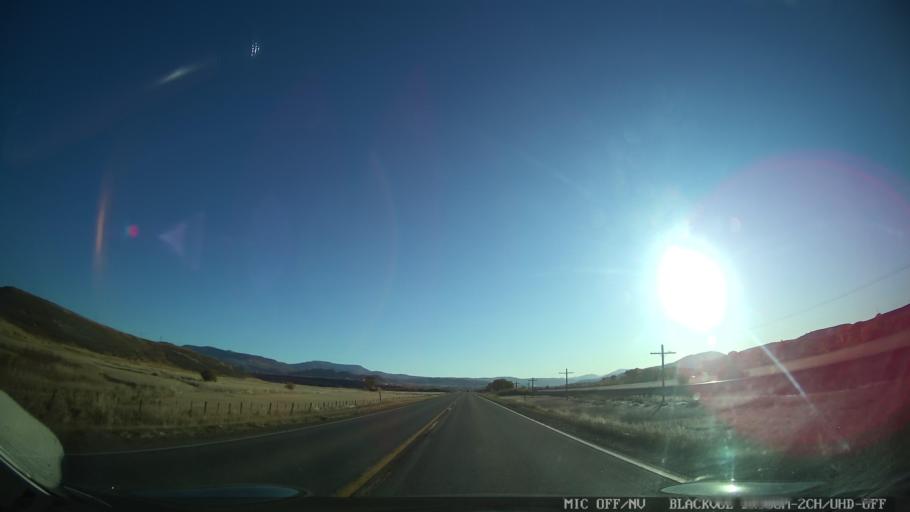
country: US
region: Colorado
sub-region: Grand County
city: Kremmling
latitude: 40.0570
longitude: -106.3135
